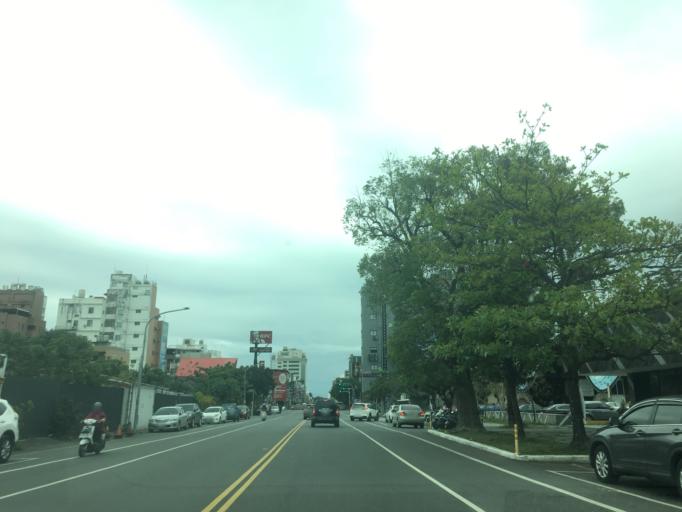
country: TW
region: Taiwan
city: Taitung City
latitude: 22.7539
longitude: 121.1466
